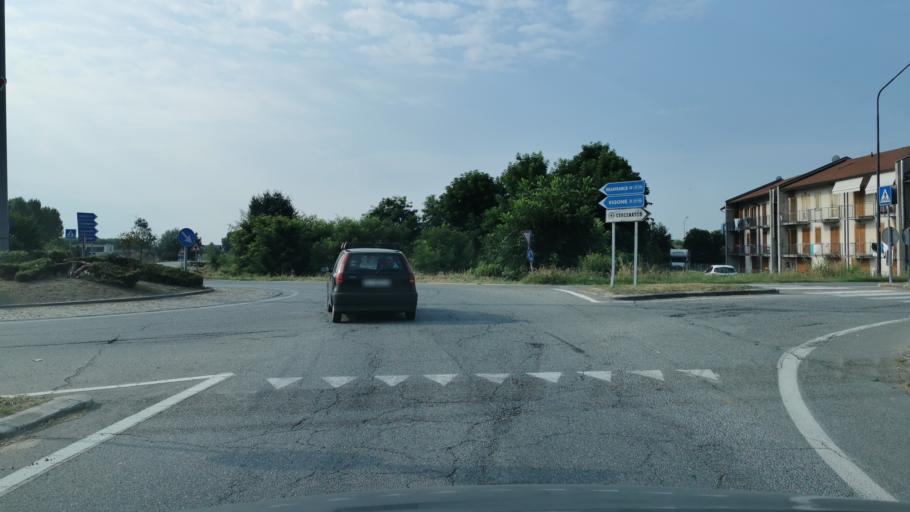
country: IT
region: Piedmont
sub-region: Provincia di Torino
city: Cercenasco
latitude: 44.8618
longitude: 7.5096
